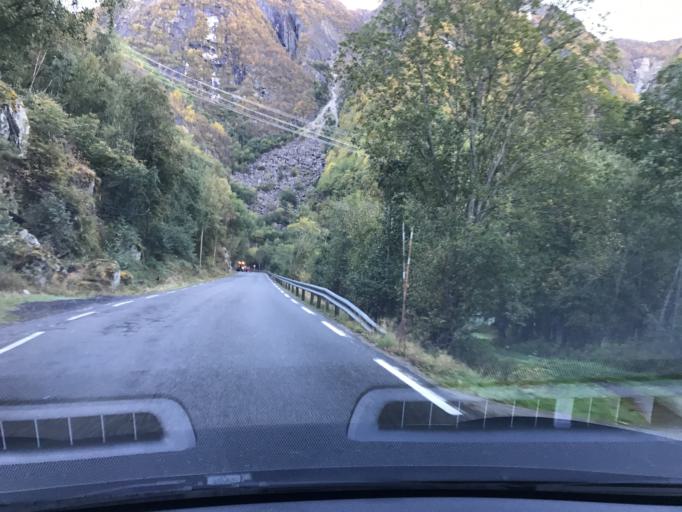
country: NO
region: Sogn og Fjordane
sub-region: Aurland
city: Aurlandsvangen
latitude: 60.8625
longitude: 7.3049
